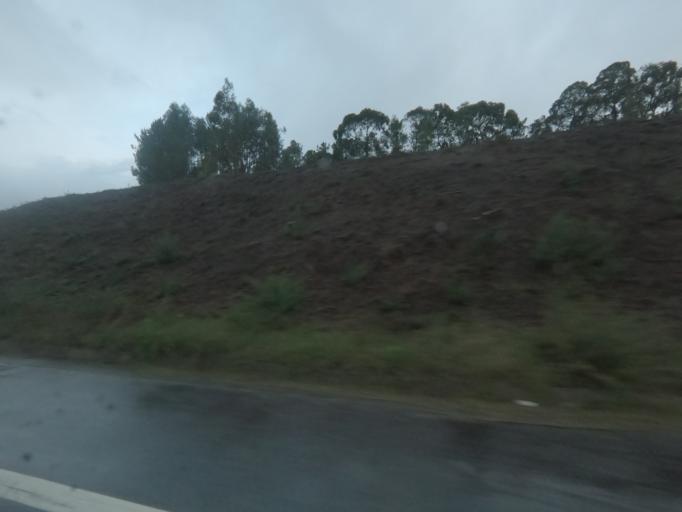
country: PT
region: Braga
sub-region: Vila Verde
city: Prado
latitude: 41.5412
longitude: -8.4959
